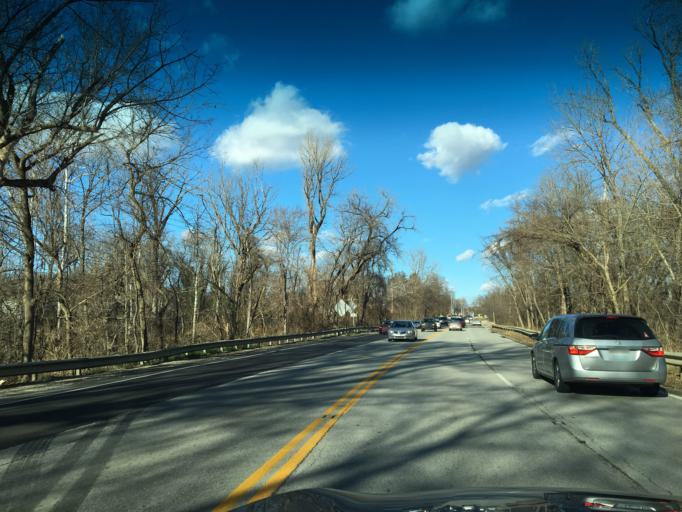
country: US
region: Kentucky
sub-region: Jefferson County
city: Prospect
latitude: 38.3318
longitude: -85.6228
